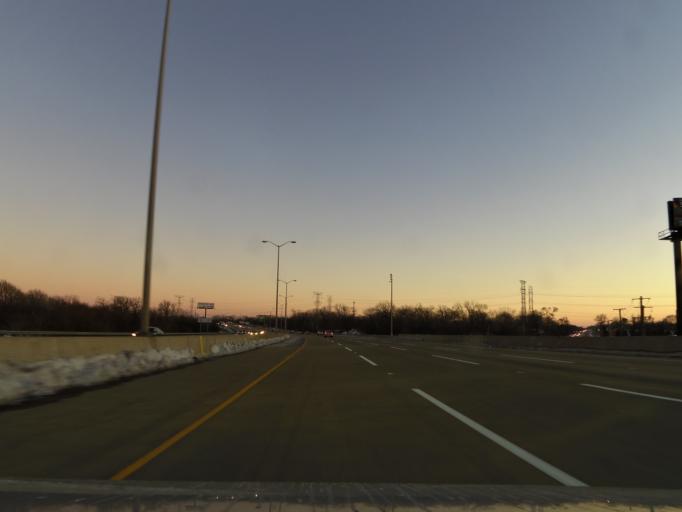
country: US
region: Illinois
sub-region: Cook County
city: Midlothian
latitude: 41.6387
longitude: -87.7178
